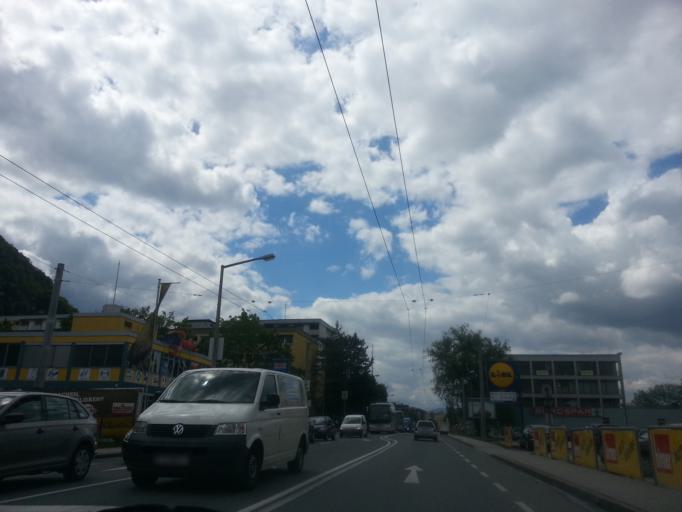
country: AT
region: Salzburg
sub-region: Salzburg Stadt
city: Salzburg
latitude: 47.8095
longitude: 13.0600
